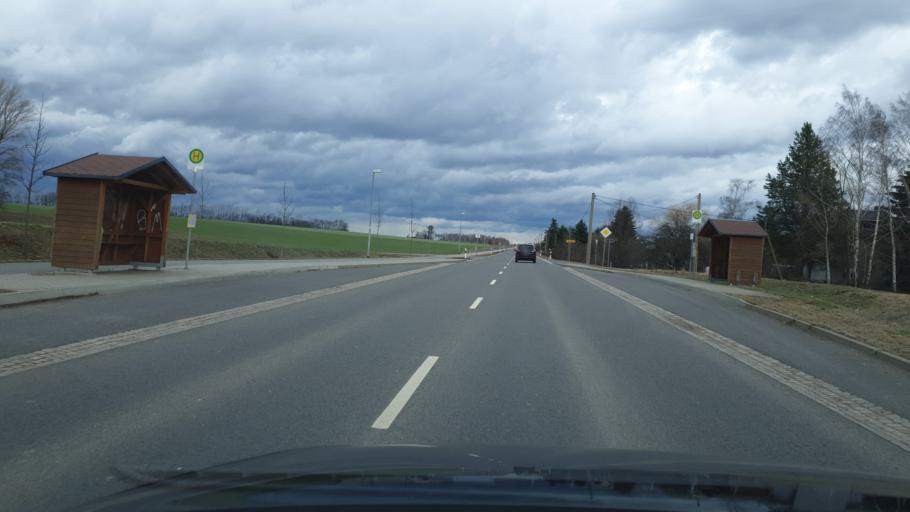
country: DE
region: Saxony
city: Claussnitz
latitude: 50.9462
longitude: 12.9024
